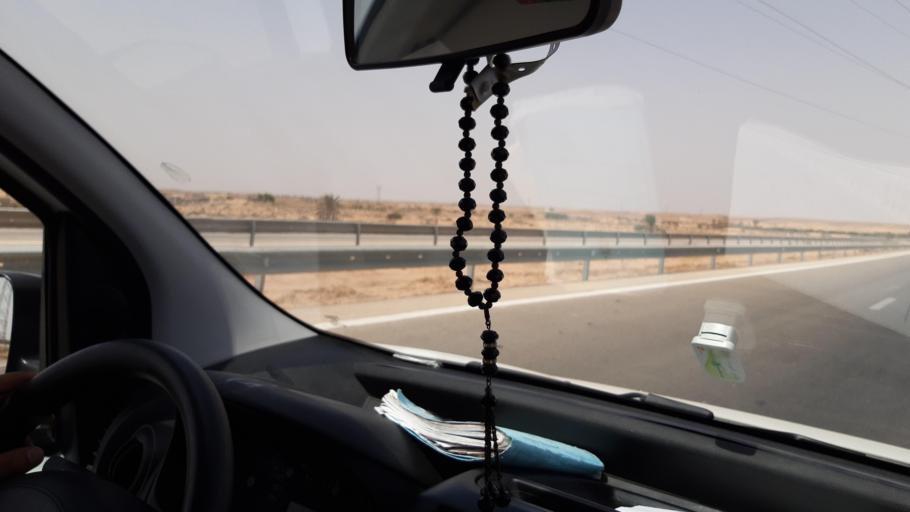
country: TN
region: Safaqis
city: Skhira
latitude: 34.1842
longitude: 9.9772
